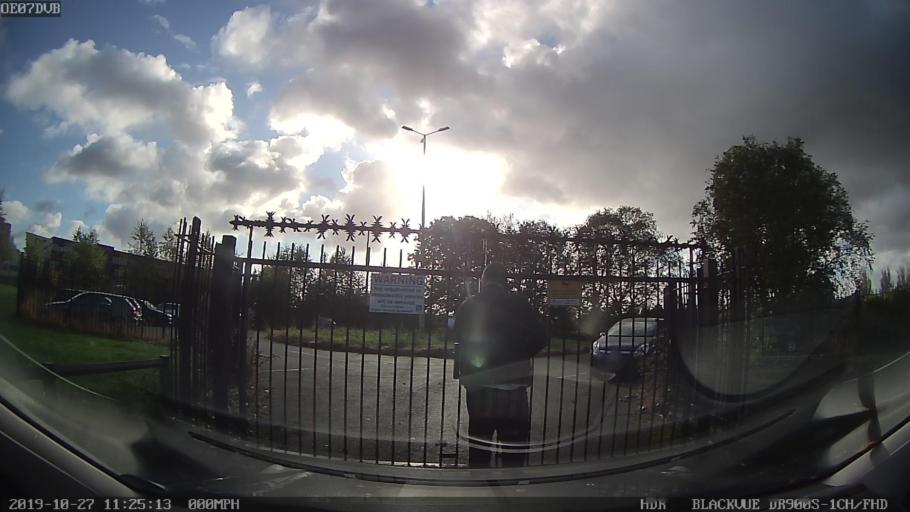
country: GB
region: England
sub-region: Borough of Rochdale
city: Middleton
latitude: 53.5273
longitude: -2.1904
